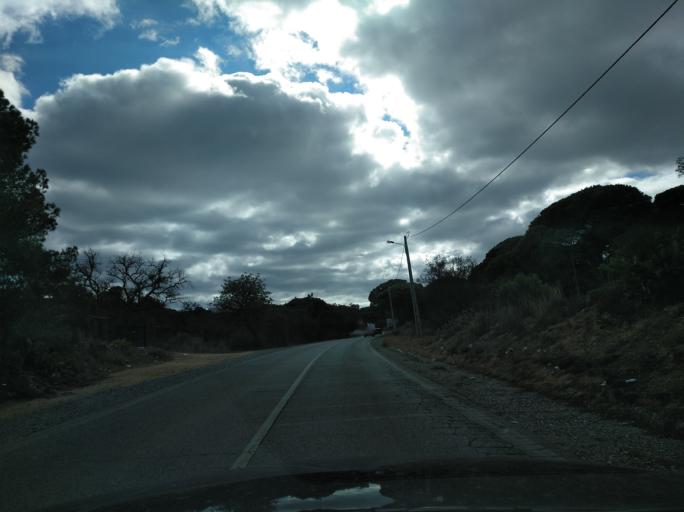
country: PT
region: Faro
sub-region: Vila Real de Santo Antonio
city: Monte Gordo
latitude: 37.1870
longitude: -7.4844
